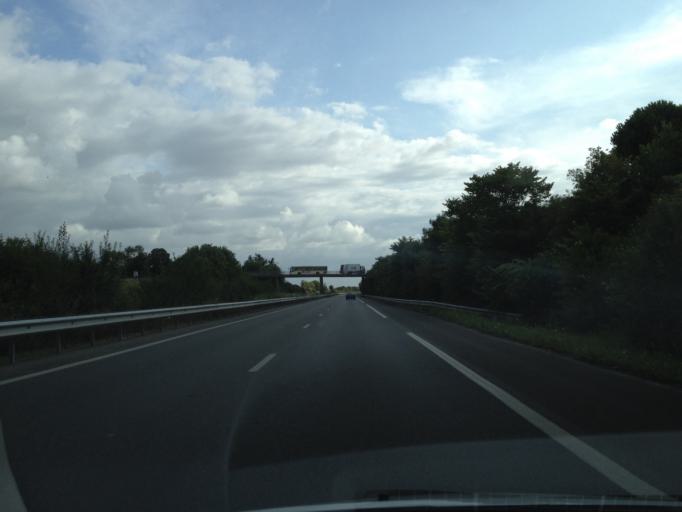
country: FR
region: Poitou-Charentes
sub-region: Departement de la Charente-Maritime
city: Dompierre-sur-Mer
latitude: 46.1886
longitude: -1.0731
